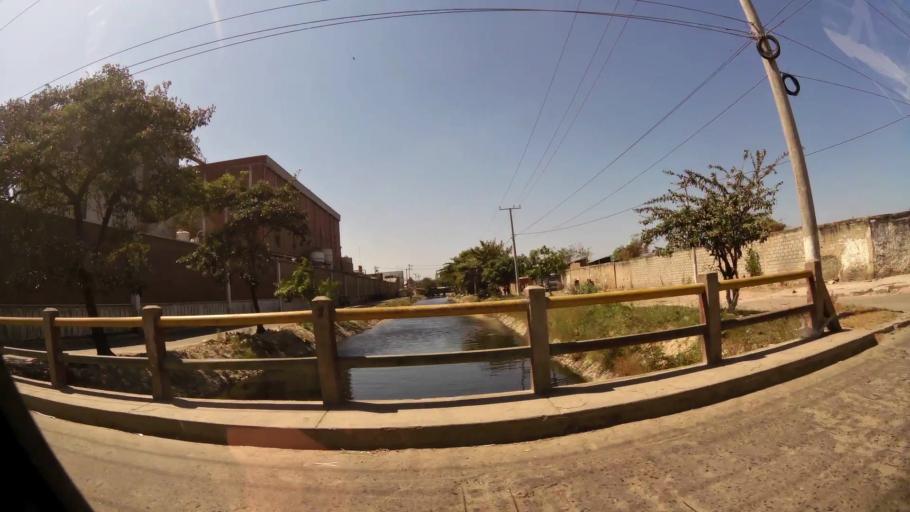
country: CO
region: Atlantico
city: Barranquilla
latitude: 10.9776
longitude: -74.7719
